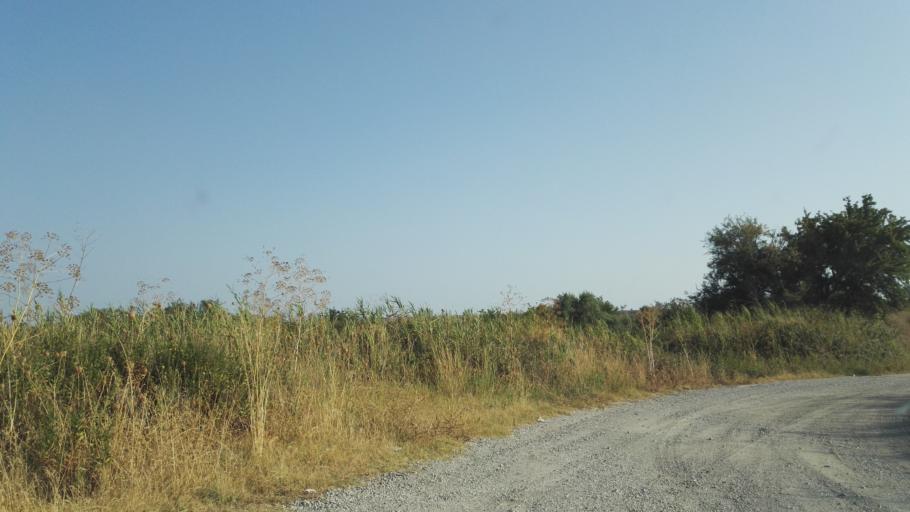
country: IT
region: Calabria
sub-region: Provincia di Reggio Calabria
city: Riace Marina
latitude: 38.3722
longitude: 16.5068
